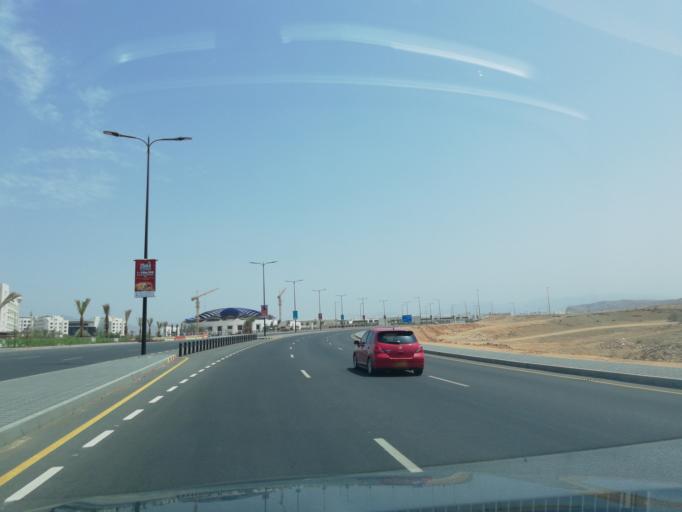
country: OM
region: Muhafazat Masqat
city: Bawshar
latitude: 23.5756
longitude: 58.3252
